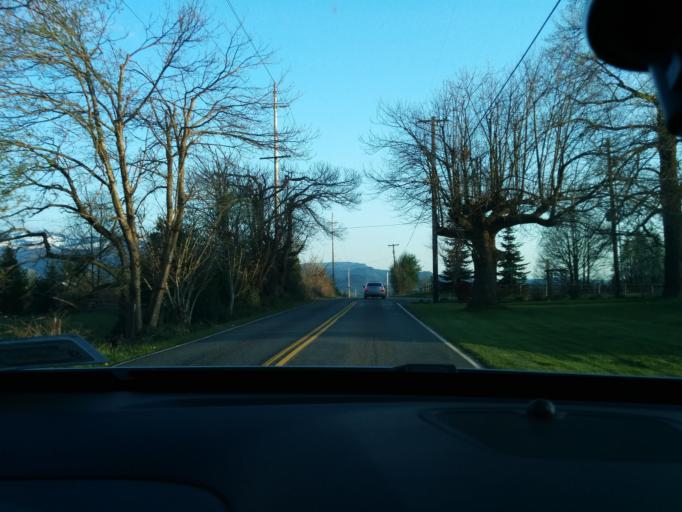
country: US
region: Washington
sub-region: Snohomish County
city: Sultan
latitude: 47.8934
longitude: -121.7991
